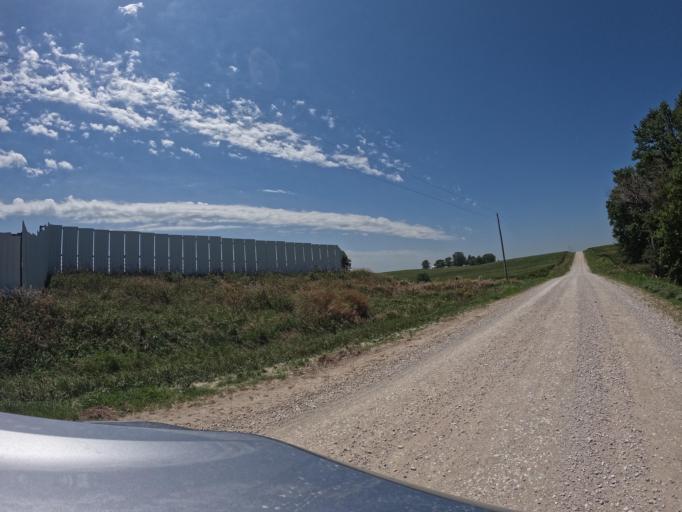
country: US
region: Iowa
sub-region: Poweshiek County
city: Montezuma
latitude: 41.4666
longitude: -92.3690
